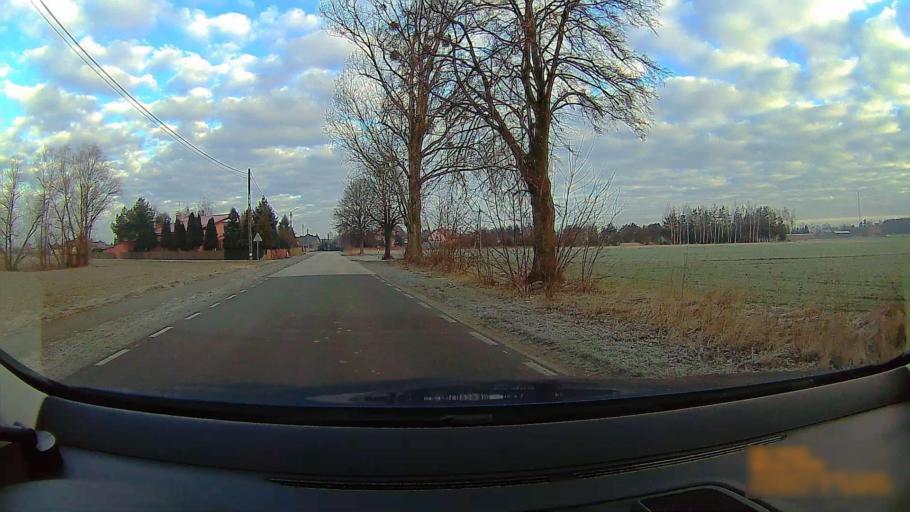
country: PL
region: Greater Poland Voivodeship
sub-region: Powiat koninski
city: Rzgow Pierwszy
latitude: 52.1488
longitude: 18.0536
